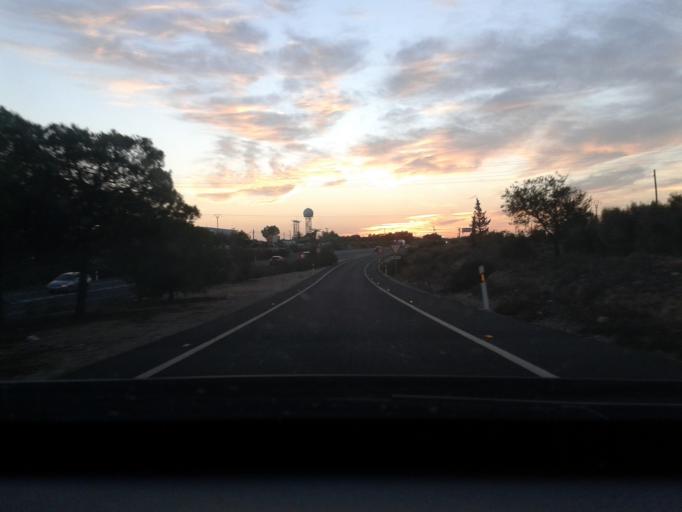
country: ES
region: Valencia
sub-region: Provincia de Alicante
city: Alicante
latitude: 38.2907
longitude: -0.5593
